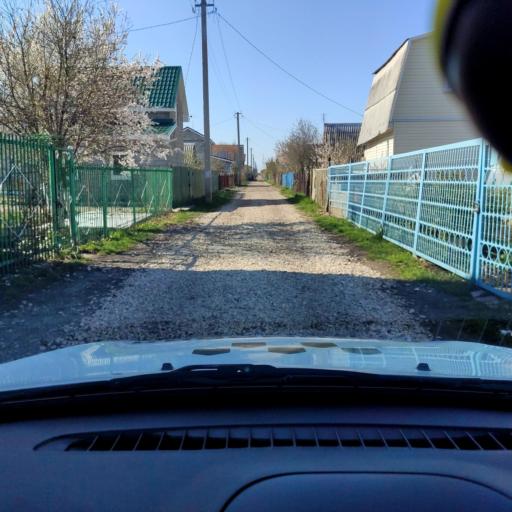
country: RU
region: Samara
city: Tol'yatti
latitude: 53.5986
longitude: 49.2951
